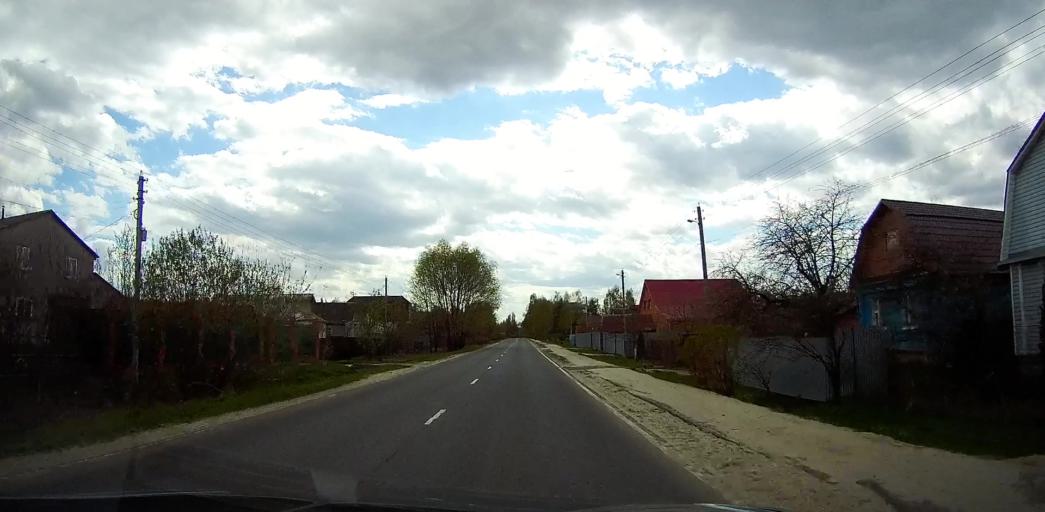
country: RU
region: Moskovskaya
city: Davydovo
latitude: 55.6633
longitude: 38.7573
